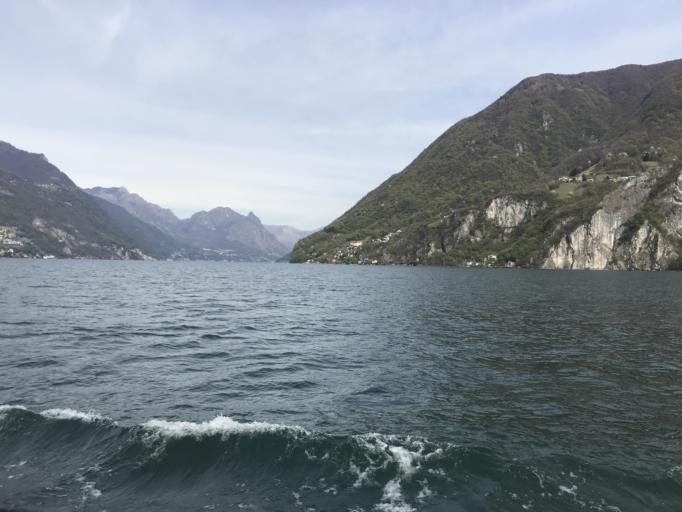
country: IT
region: Lombardy
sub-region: Provincia di Como
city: Campione
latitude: 45.9780
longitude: 8.9607
